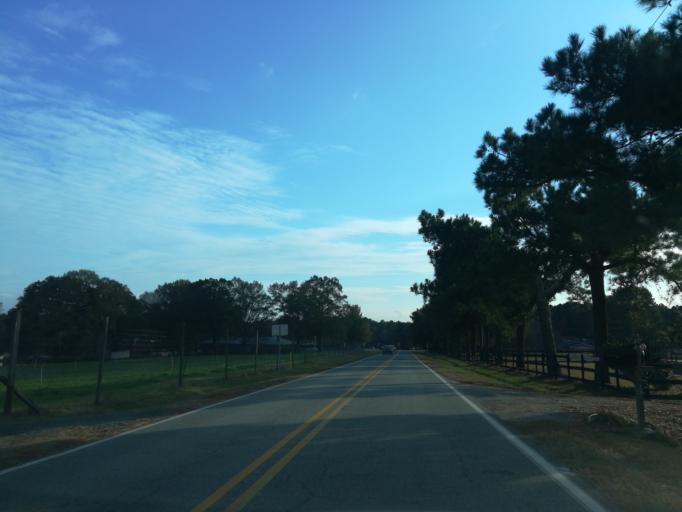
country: US
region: North Carolina
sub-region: Durham County
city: Durham
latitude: 35.9919
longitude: -78.9941
